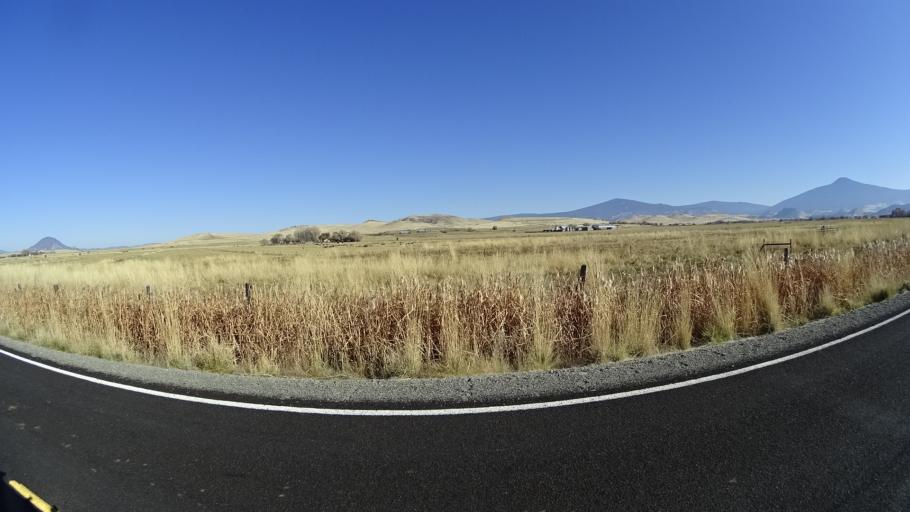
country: US
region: California
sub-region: Siskiyou County
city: Montague
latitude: 41.7183
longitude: -122.4492
